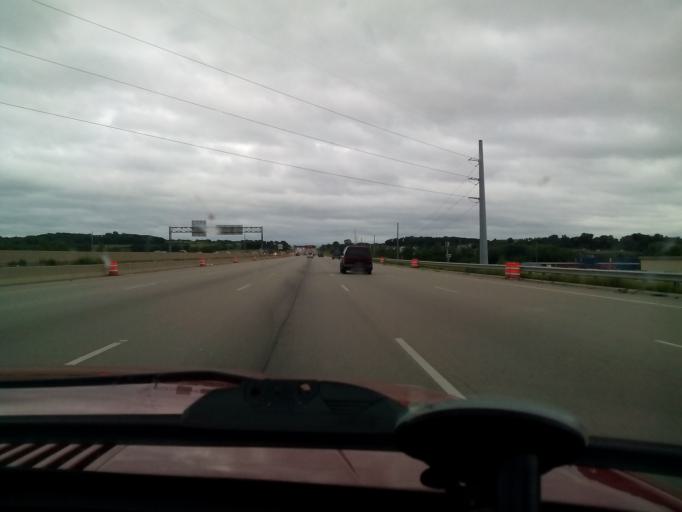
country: US
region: Wisconsin
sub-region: Dane County
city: Monona
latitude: 43.1286
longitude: -89.2920
